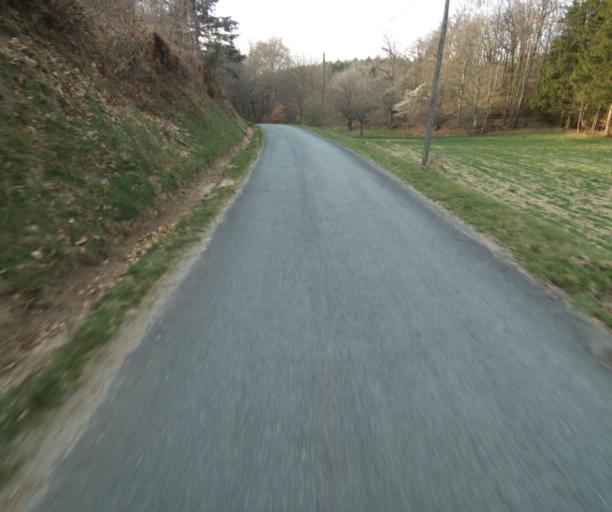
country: FR
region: Limousin
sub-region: Departement de la Correze
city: Correze
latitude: 45.3808
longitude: 1.8598
